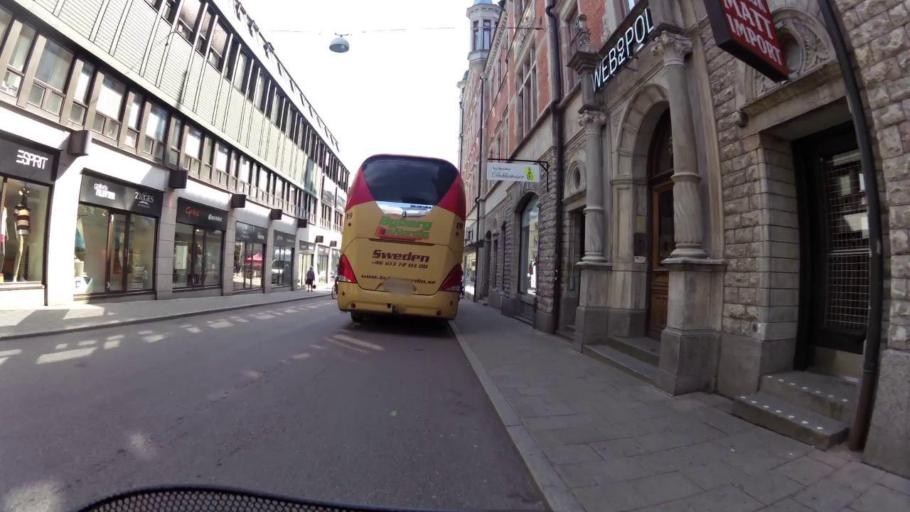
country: SE
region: OEstergoetland
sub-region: Linkopings Kommun
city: Linkoping
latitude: 58.4105
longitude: 15.6203
